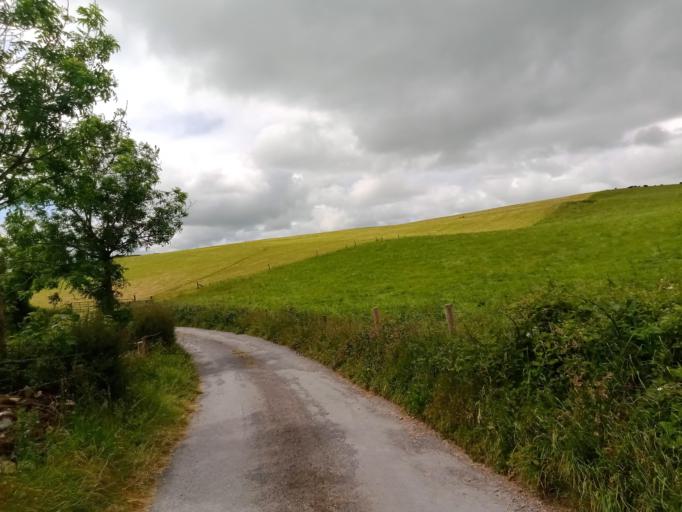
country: IE
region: Leinster
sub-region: Laois
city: Rathdowney
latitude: 52.7940
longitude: -7.4722
